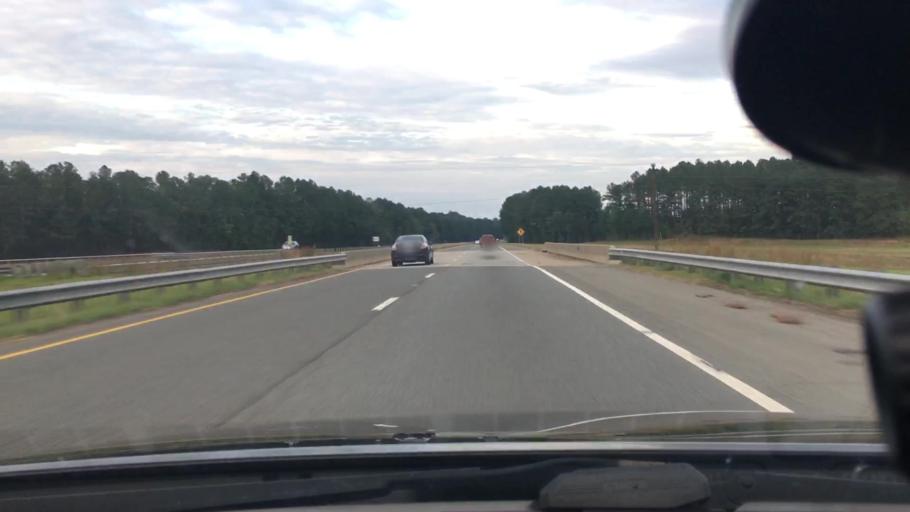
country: US
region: North Carolina
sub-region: Chatham County
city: Farmville
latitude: 35.5607
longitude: -79.1533
